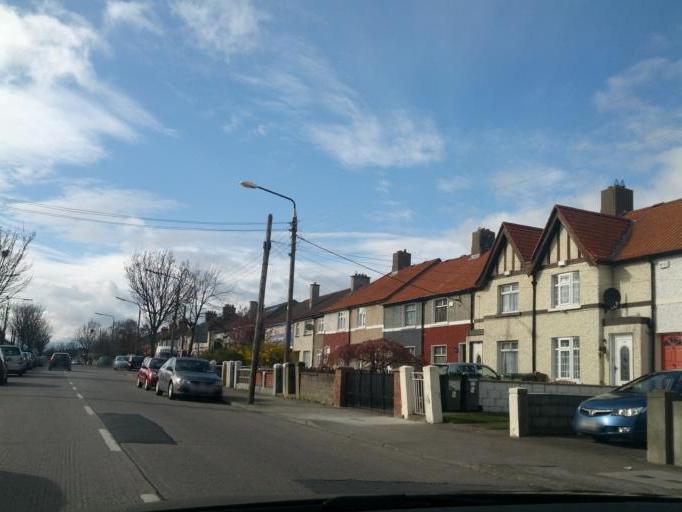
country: IE
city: Donnycarney
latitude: 53.3766
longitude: -6.2221
